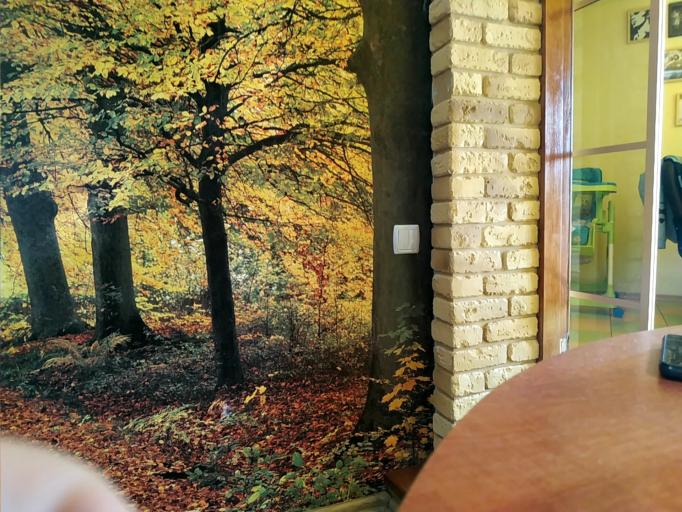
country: RU
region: Novgorod
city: Parfino
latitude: 57.8060
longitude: 31.5903
